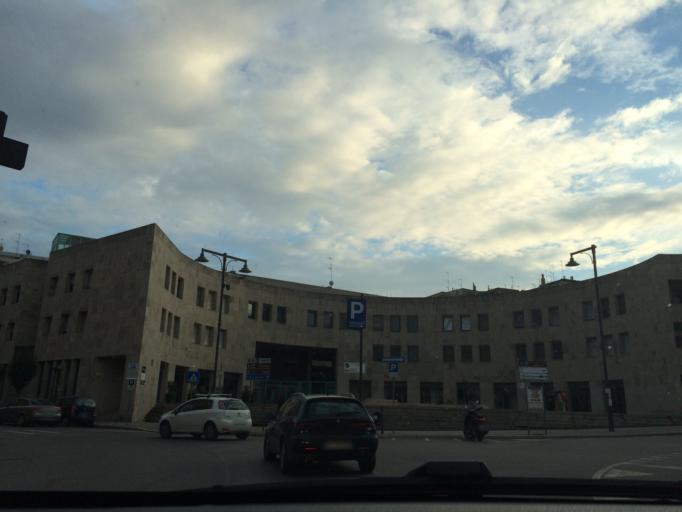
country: IT
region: Basilicate
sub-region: Provincia di Matera
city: Matera
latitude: 40.6665
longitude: 16.6044
